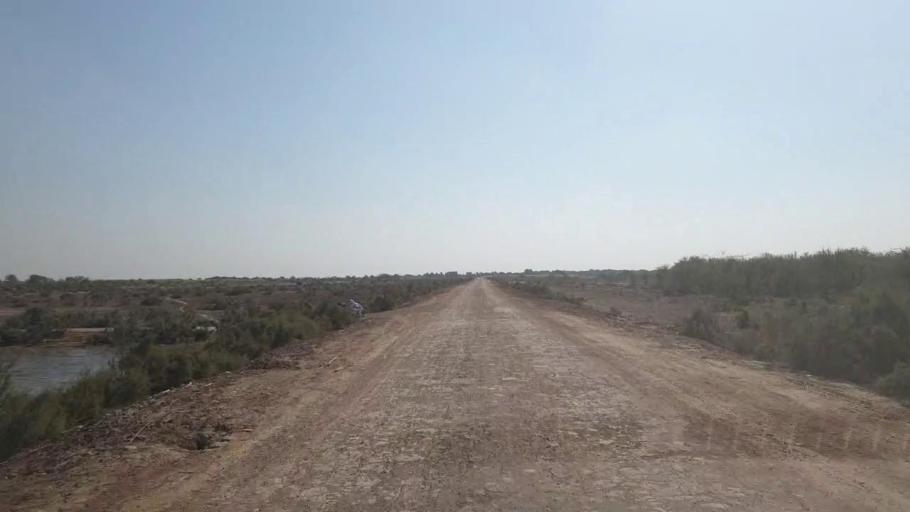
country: PK
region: Sindh
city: Chambar
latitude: 25.3267
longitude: 68.7399
